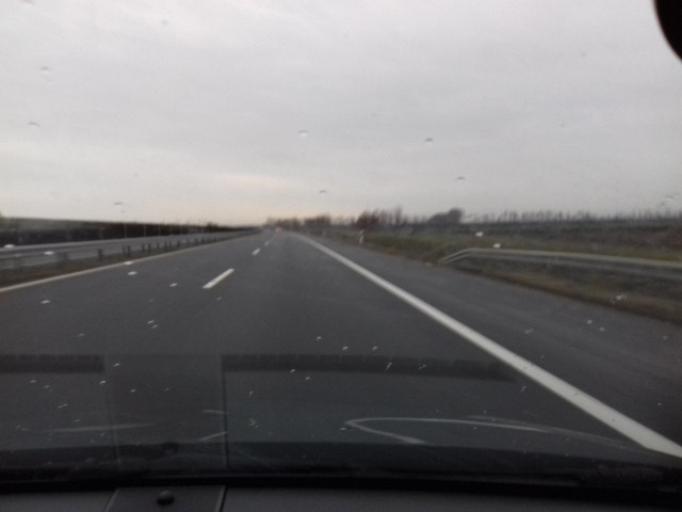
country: HU
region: Hajdu-Bihar
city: Hajduboszormeny
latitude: 47.6290
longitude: 21.5109
